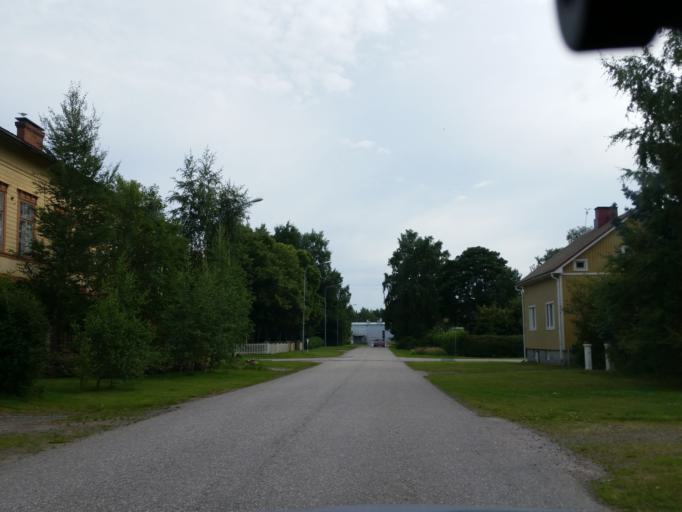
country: FI
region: Uusimaa
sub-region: Raaseporin
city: Hanko
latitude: 59.8307
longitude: 22.9536
